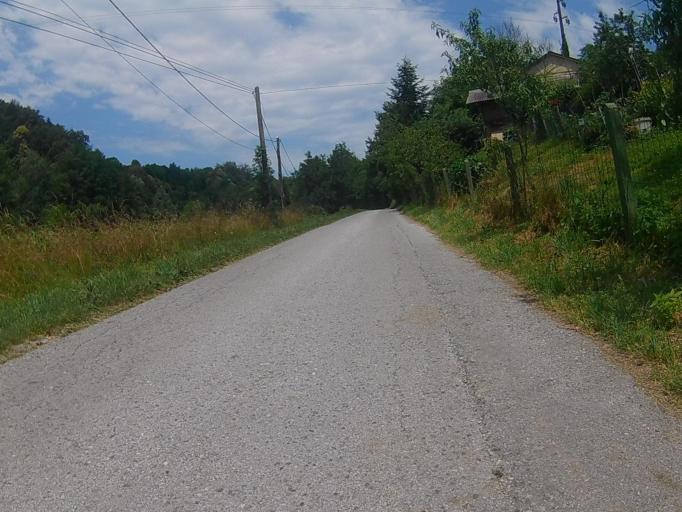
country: SI
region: Maribor
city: Kamnica
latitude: 46.5925
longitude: 15.6270
